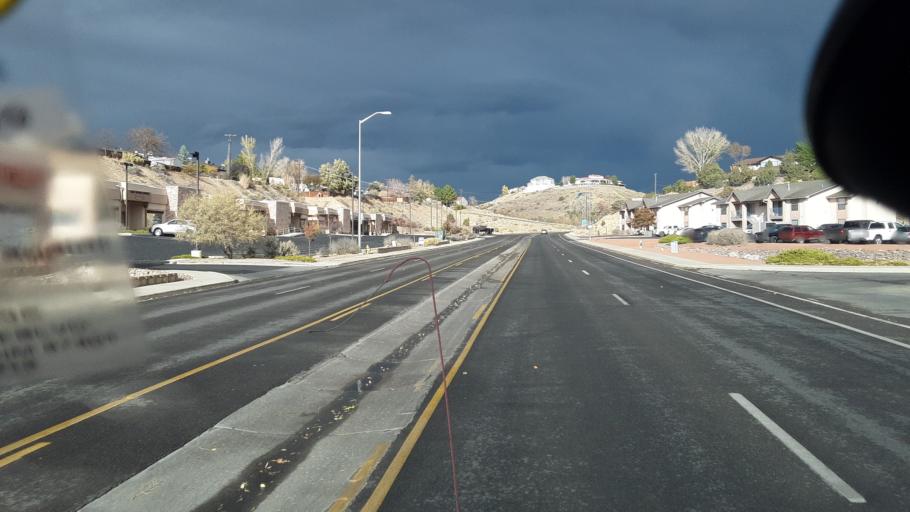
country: US
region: New Mexico
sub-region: San Juan County
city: Farmington
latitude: 36.7592
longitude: -108.1952
